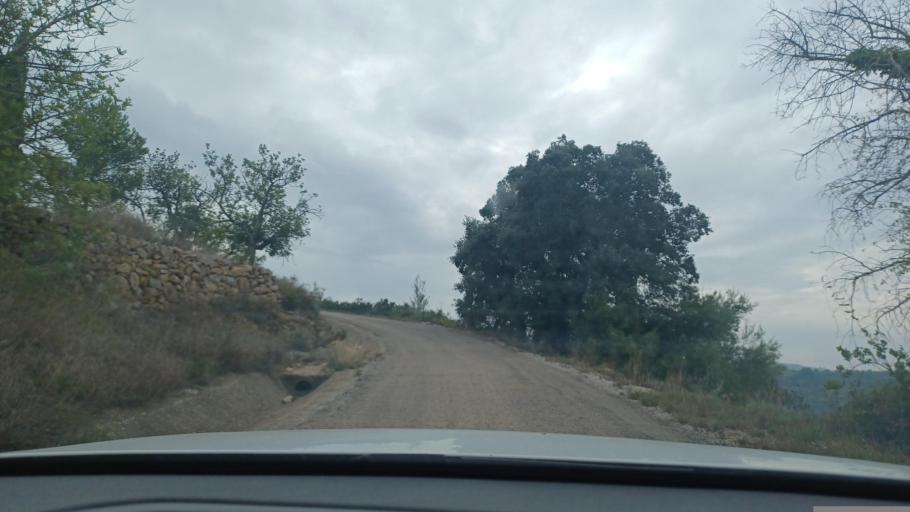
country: ES
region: Catalonia
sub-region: Provincia de Tarragona
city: Ulldecona
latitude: 40.6492
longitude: 0.4701
